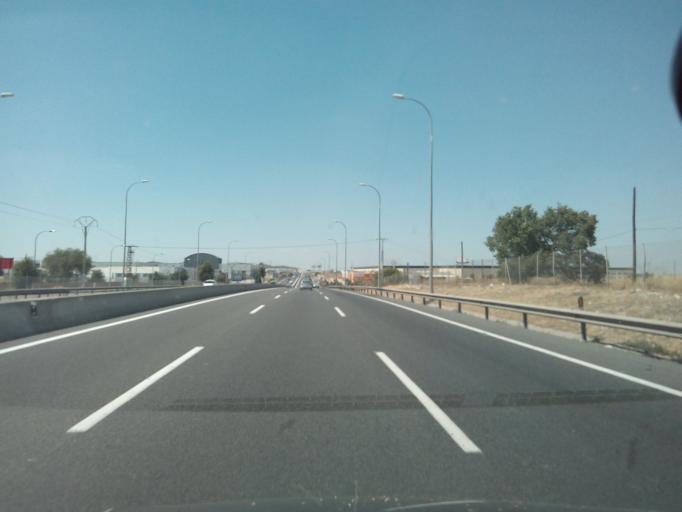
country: ES
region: Castille-La Mancha
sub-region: Province of Toledo
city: Sesena
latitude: 40.1108
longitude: -3.6491
